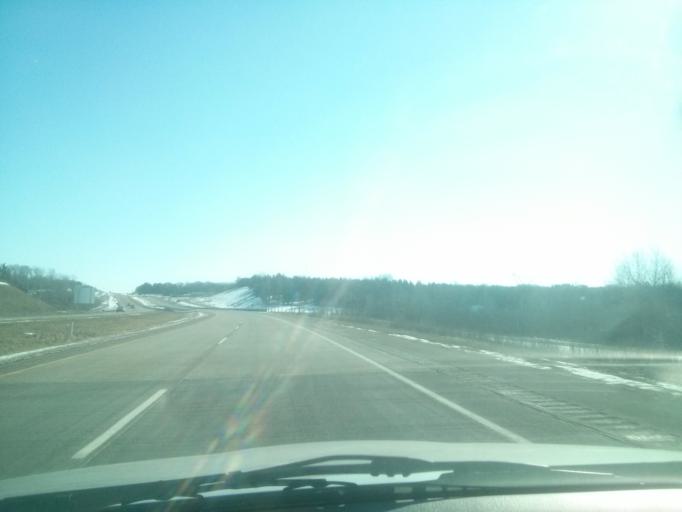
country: US
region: Wisconsin
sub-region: Saint Croix County
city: Somerset
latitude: 45.1233
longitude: -92.6387
